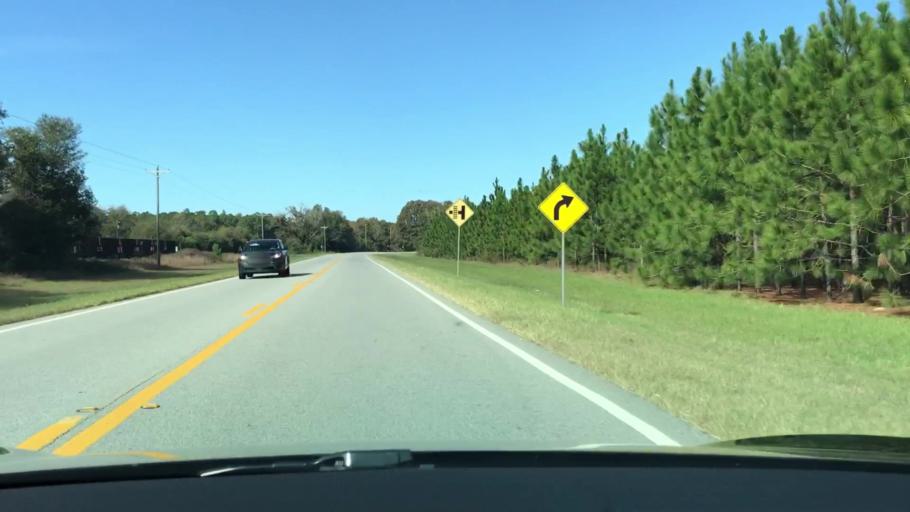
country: US
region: Georgia
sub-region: Glascock County
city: Gibson
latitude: 33.3070
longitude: -82.5297
